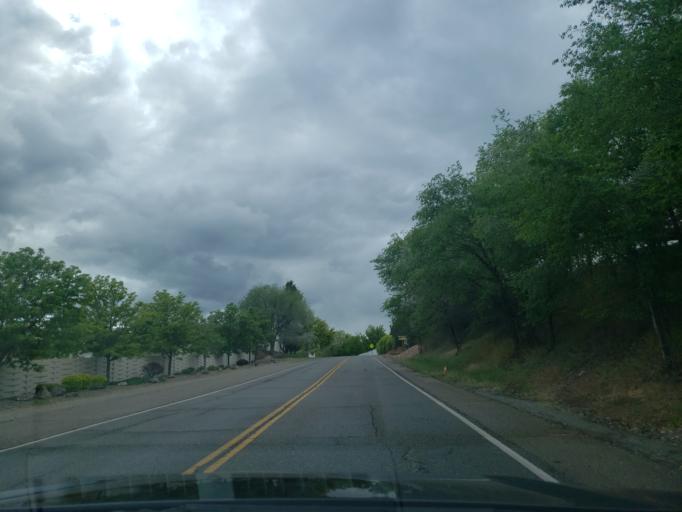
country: US
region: Colorado
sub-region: Mesa County
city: Redlands
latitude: 39.0819
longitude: -108.6333
